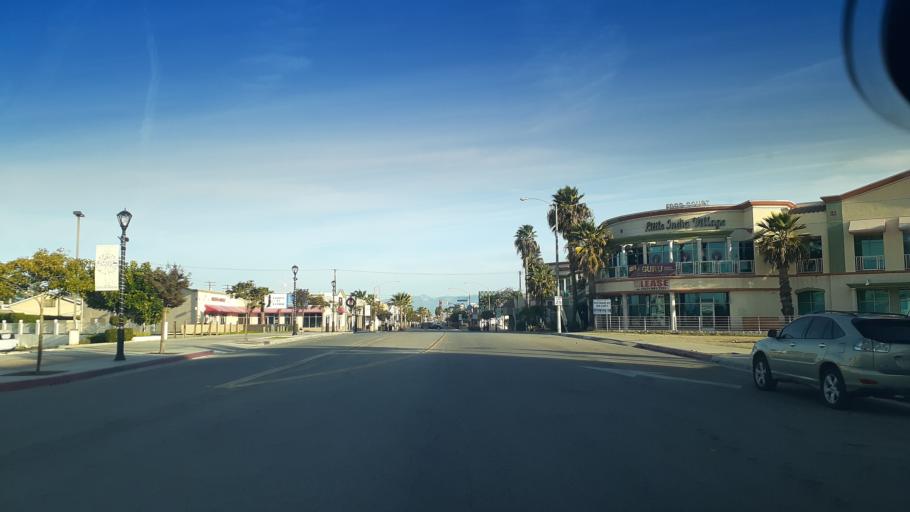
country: US
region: California
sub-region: Los Angeles County
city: Artesia
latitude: 33.8600
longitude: -118.0822
